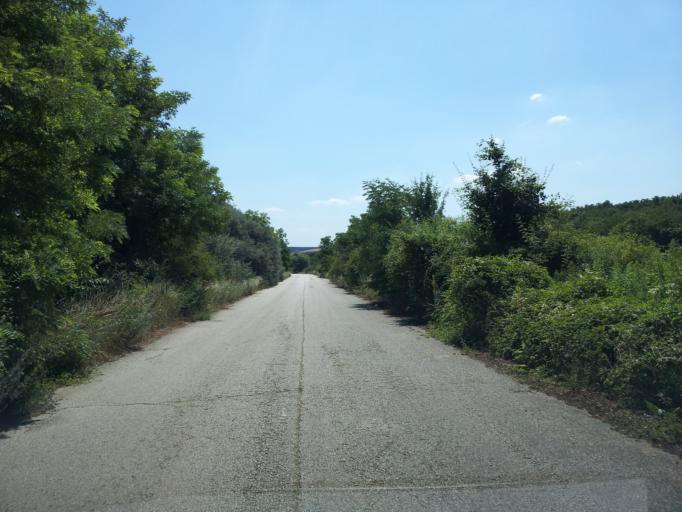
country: HU
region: Fejer
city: Szarliget
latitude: 47.5268
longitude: 18.5653
